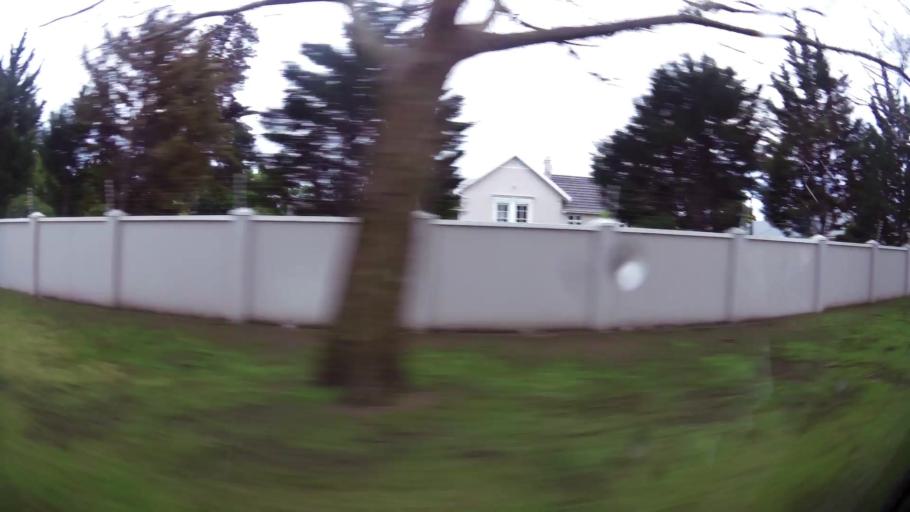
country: ZA
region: Eastern Cape
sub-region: Nelson Mandela Bay Metropolitan Municipality
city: Port Elizabeth
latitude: -33.9782
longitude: 25.5678
